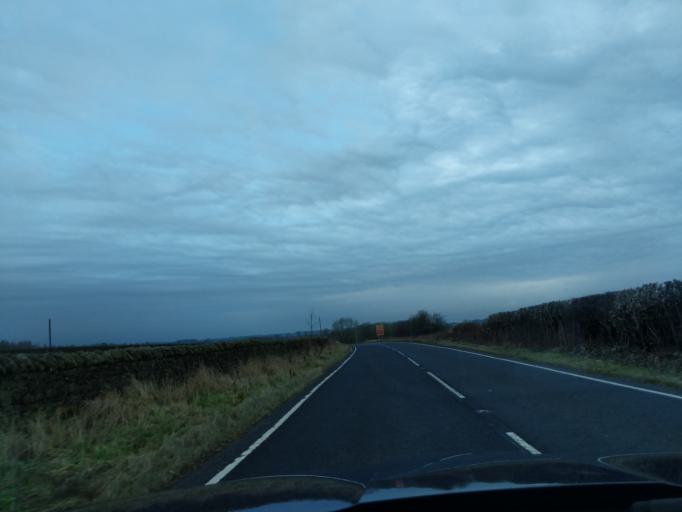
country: GB
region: England
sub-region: Northumberland
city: Rothley
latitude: 55.1282
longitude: -1.9378
